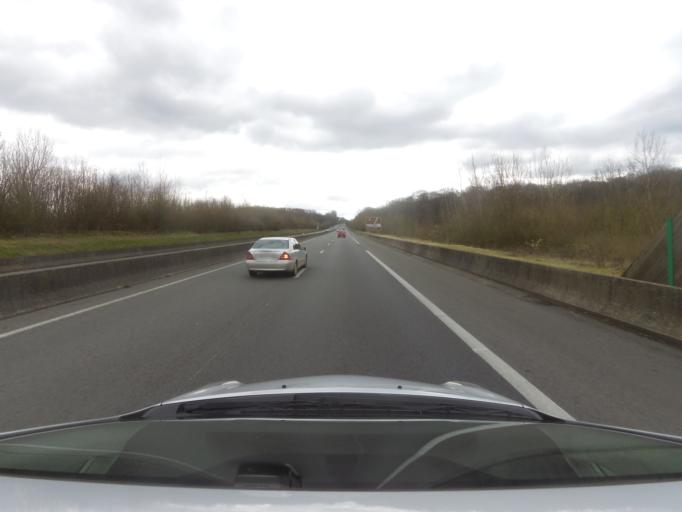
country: FR
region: Nord-Pas-de-Calais
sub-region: Departement du Pas-de-Calais
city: Saint-Josse
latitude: 50.4820
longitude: 1.6912
